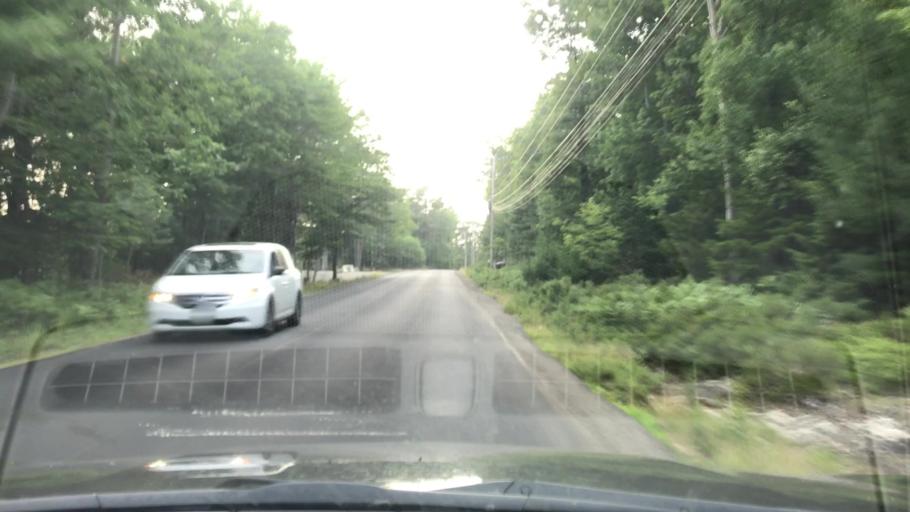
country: US
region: Maine
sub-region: Hancock County
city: Bar Harbor
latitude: 44.3659
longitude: -68.1926
